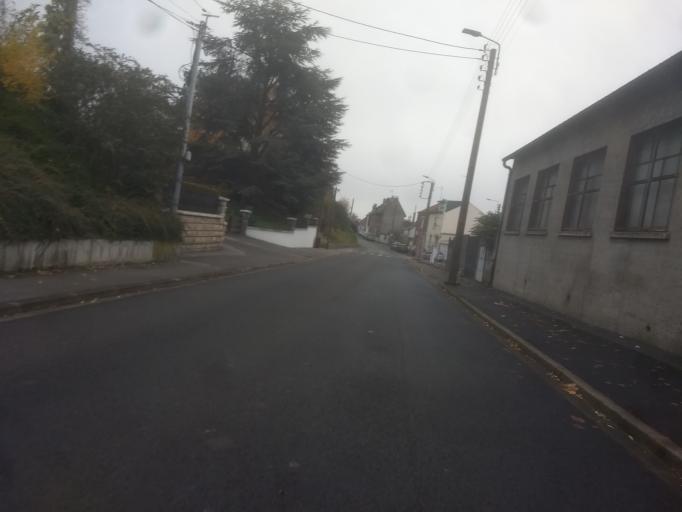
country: FR
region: Nord-Pas-de-Calais
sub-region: Departement du Pas-de-Calais
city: Saint-Laurent-Blangy
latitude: 50.3038
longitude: 2.8060
